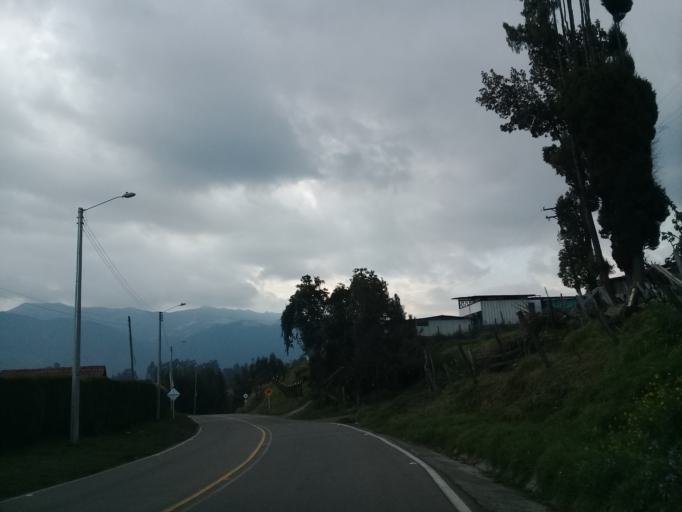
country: CO
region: Cundinamarca
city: Zipaquira
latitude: 5.0349
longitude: -74.0421
